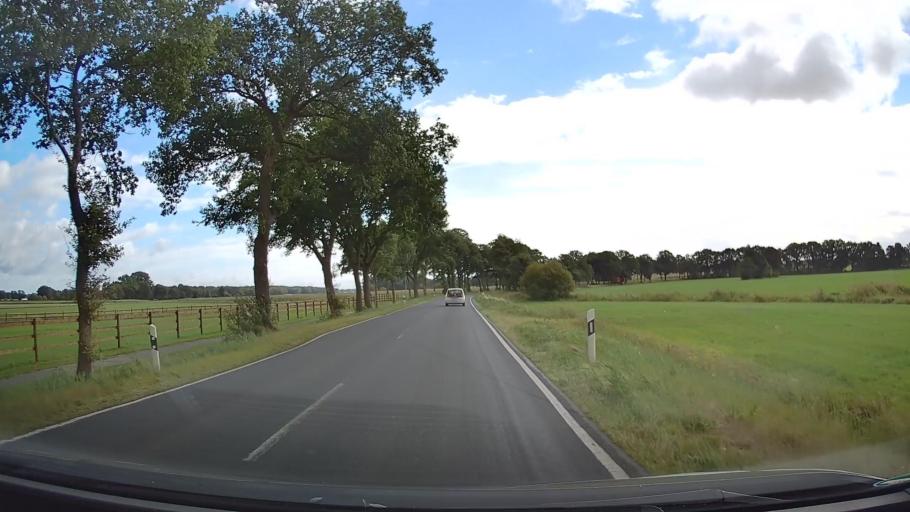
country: DE
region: Lower Saxony
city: Rhade
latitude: 53.3251
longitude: 9.1219
